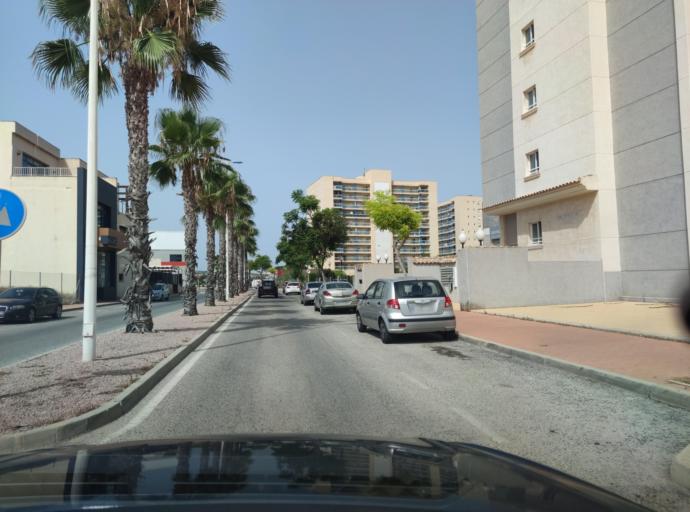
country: ES
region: Valencia
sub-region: Provincia de Alicante
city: Guardamar del Segura
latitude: 38.0963
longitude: -0.6596
